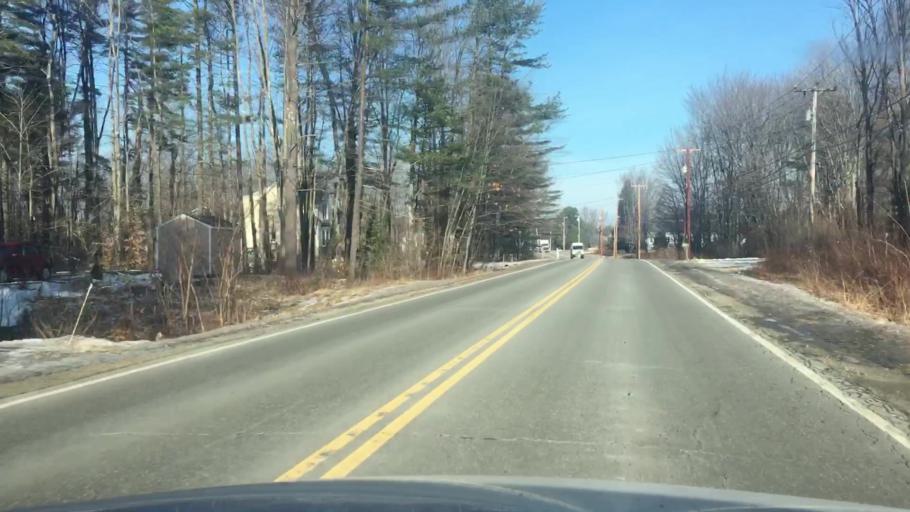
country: US
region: Maine
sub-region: Androscoggin County
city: Auburn
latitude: 44.0912
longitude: -70.2631
